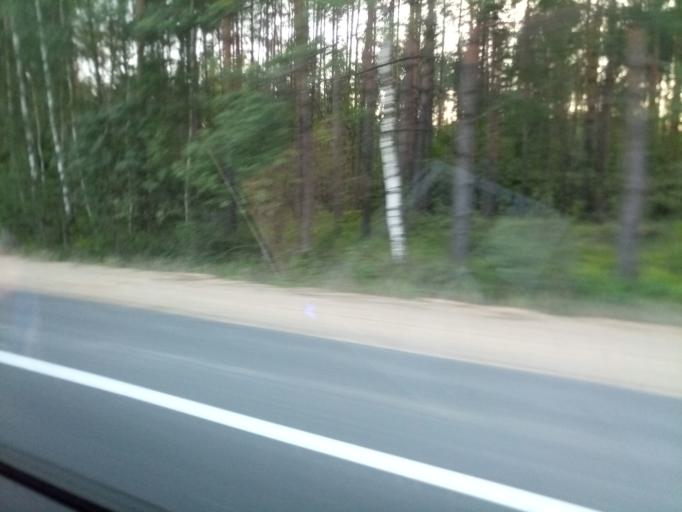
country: RU
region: Moskovskaya
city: Noginsk-9
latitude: 56.0996
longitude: 38.5842
